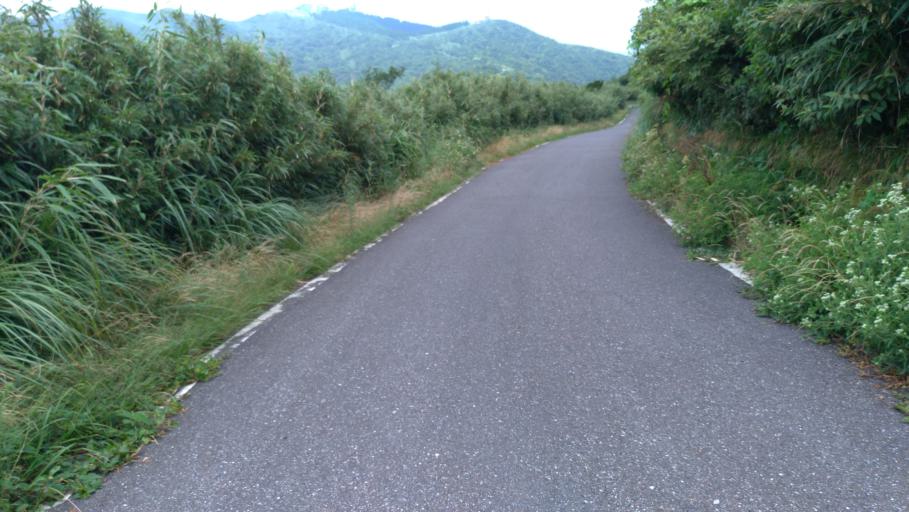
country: TW
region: Taipei
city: Taipei
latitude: 25.1827
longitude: 121.5232
